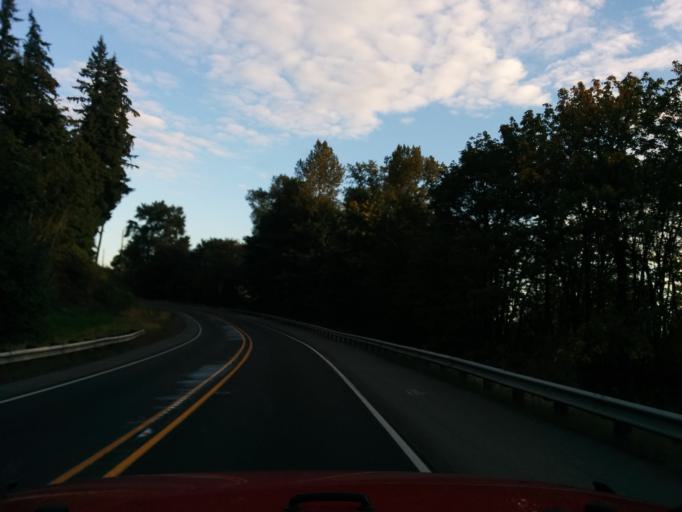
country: US
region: Washington
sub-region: King County
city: Duvall
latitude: 47.7895
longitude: -121.9745
